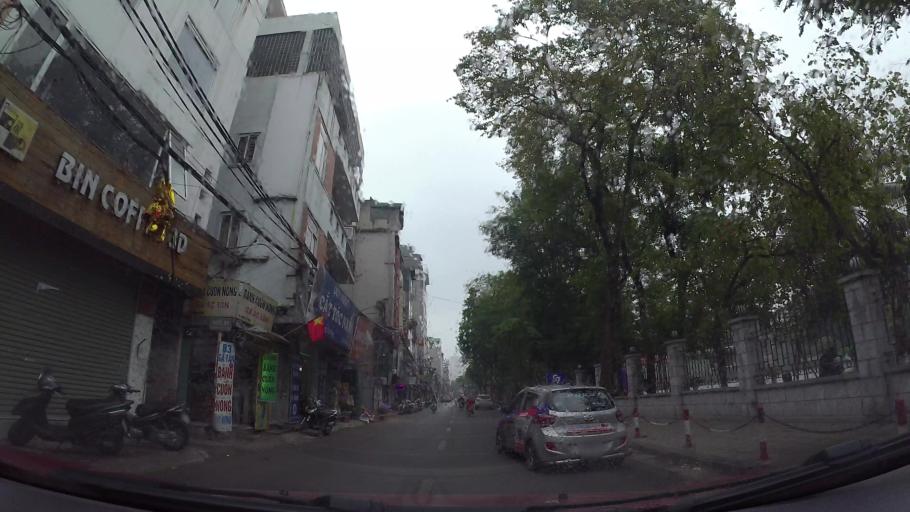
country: VN
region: Ha Noi
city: Dong Da
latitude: 21.0119
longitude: 105.8240
